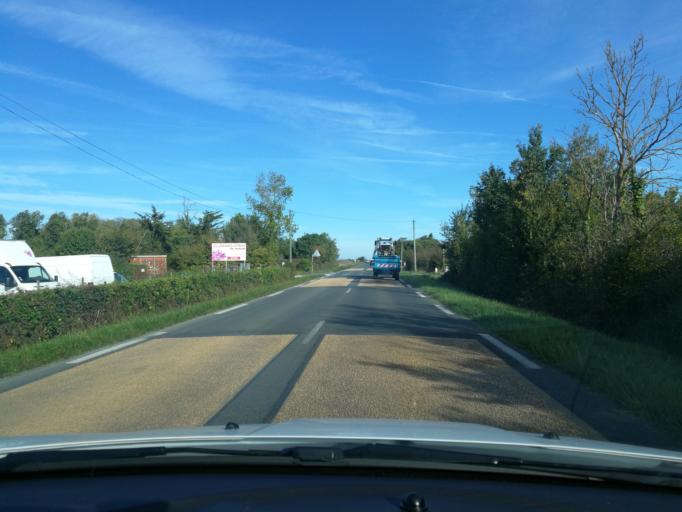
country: FR
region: Poitou-Charentes
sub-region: Departement de la Charente-Maritime
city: Saint-Denis-d'Oleron
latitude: 46.0039
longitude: -1.3673
